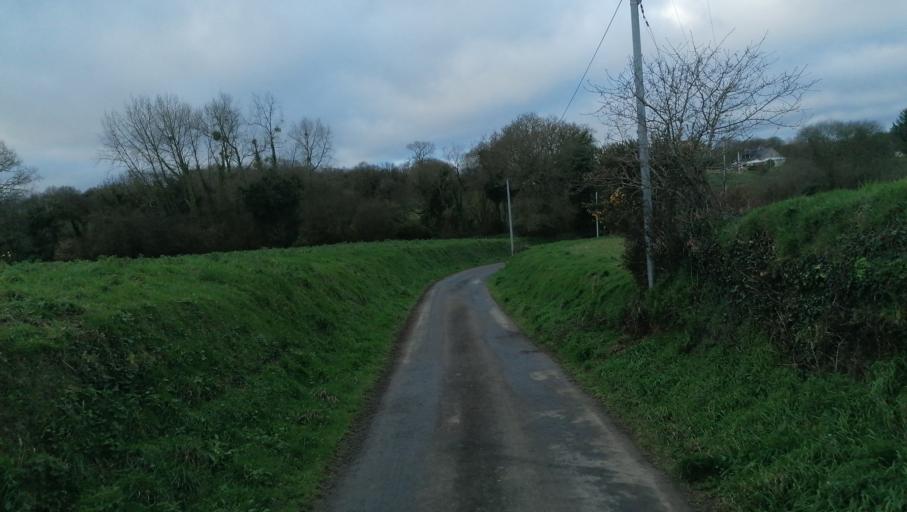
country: FR
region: Brittany
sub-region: Departement des Cotes-d'Armor
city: Pommerit-le-Vicomte
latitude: 48.6468
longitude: -3.0741
